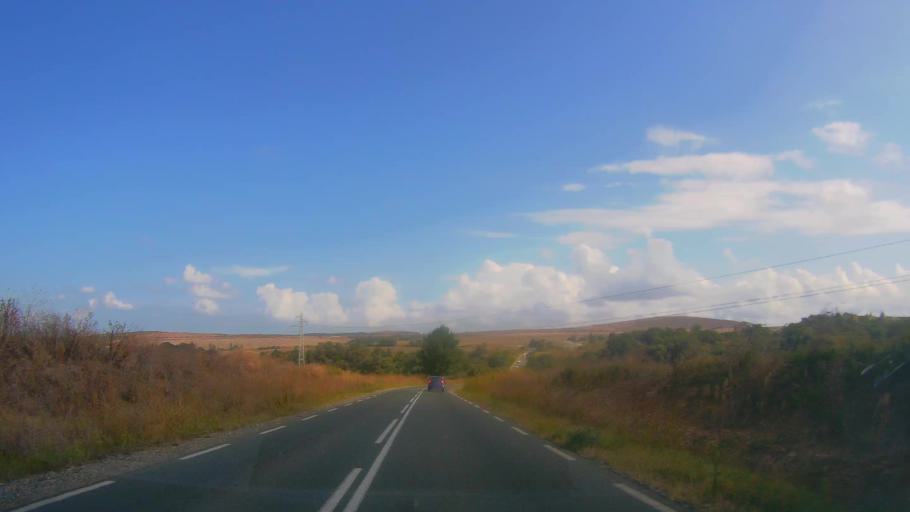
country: BG
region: Burgas
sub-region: Obshtina Kameno
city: Kameno
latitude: 42.4769
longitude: 27.3548
